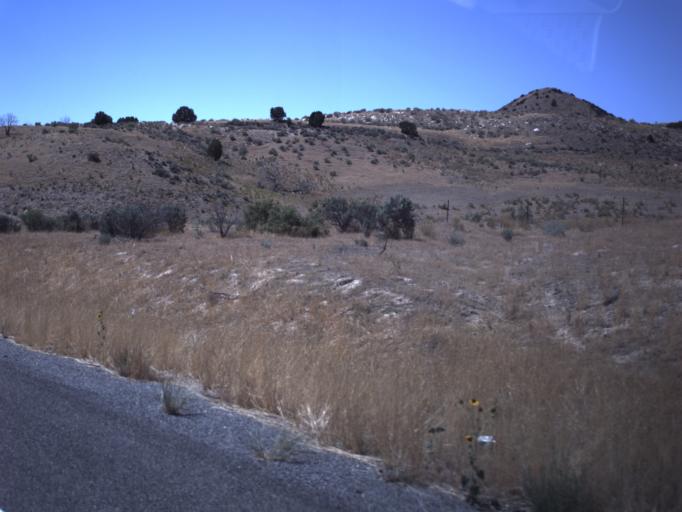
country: US
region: Utah
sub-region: Juab County
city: Nephi
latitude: 39.6014
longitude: -112.1434
